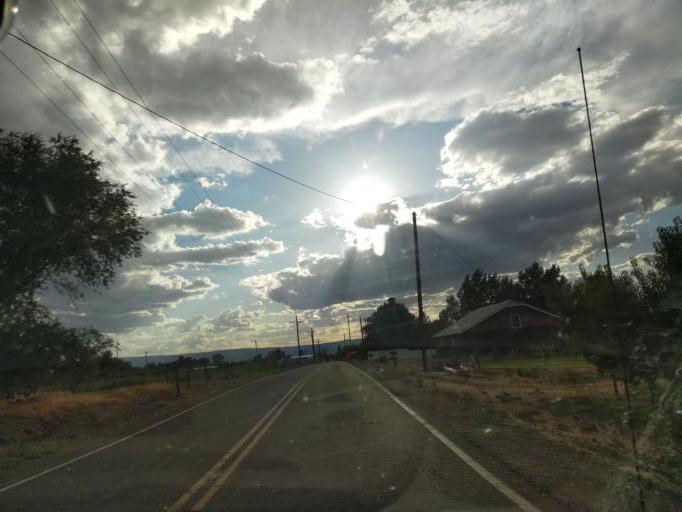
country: US
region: Colorado
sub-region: Mesa County
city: Clifton
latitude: 39.0556
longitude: -108.4154
